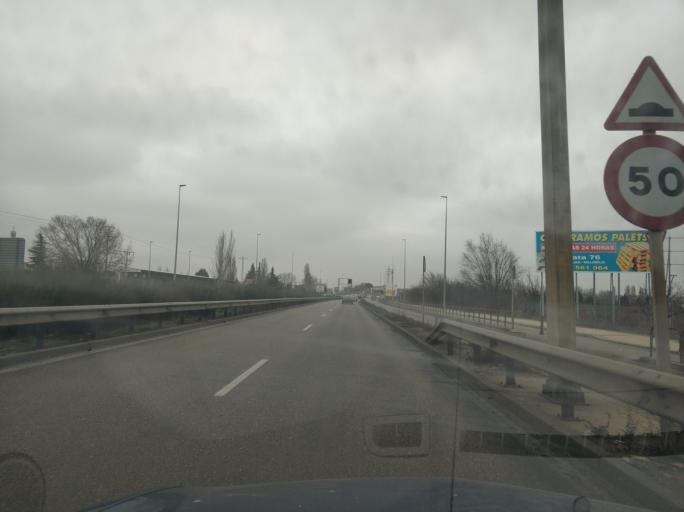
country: ES
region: Castille and Leon
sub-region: Provincia de Valladolid
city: Cisterniga
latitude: 41.6297
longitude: -4.7020
